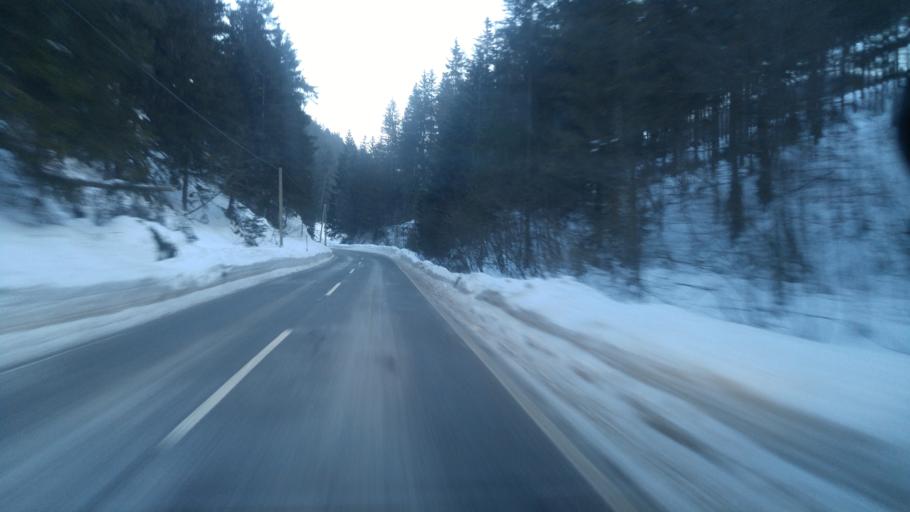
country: AT
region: Lower Austria
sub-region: Politischer Bezirk Wiener Neustadt
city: Rohr im Gebirge
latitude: 47.8752
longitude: 15.7796
